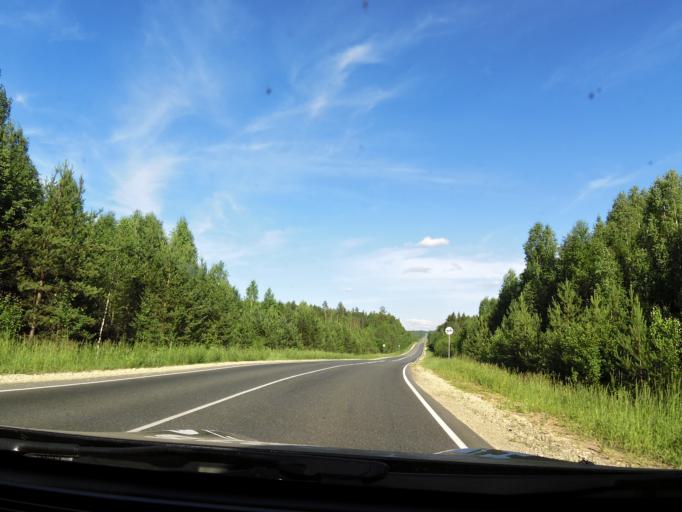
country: RU
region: Kirov
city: Dubrovka
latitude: 58.9082
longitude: 51.2474
